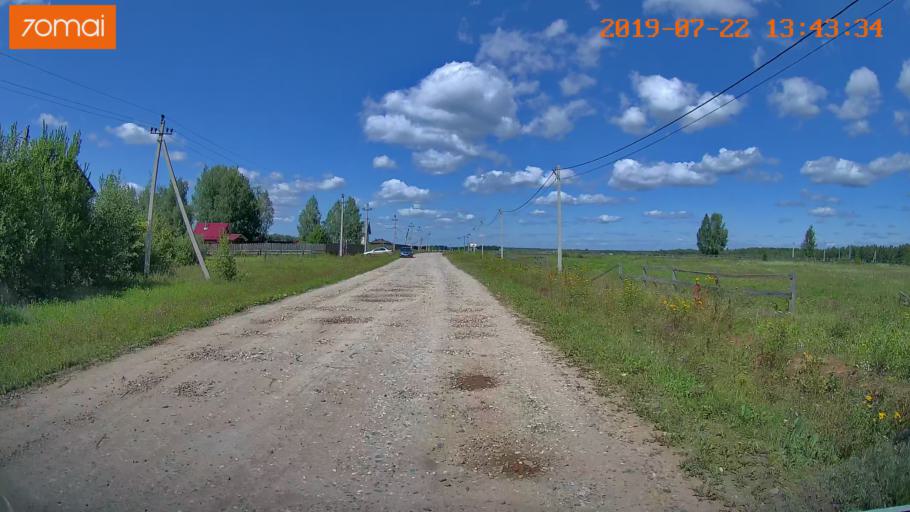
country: RU
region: Ivanovo
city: Novo-Talitsy
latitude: 57.0834
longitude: 40.8742
